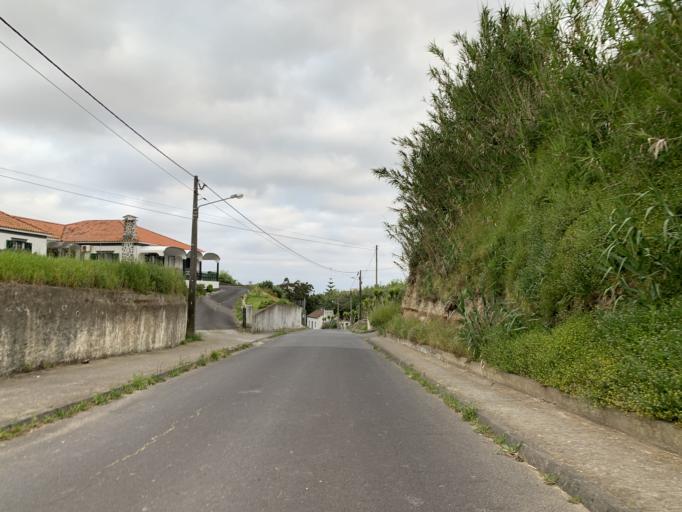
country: PT
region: Azores
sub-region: Ponta Delgada
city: Arrifes
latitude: 37.8459
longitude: -25.8400
